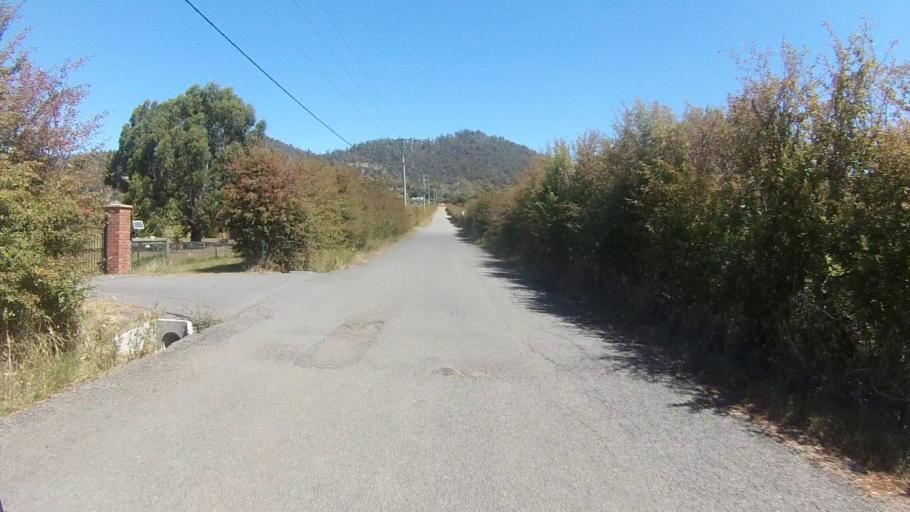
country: AU
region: Tasmania
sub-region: Clarence
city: Cambridge
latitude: -42.8441
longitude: 147.4591
